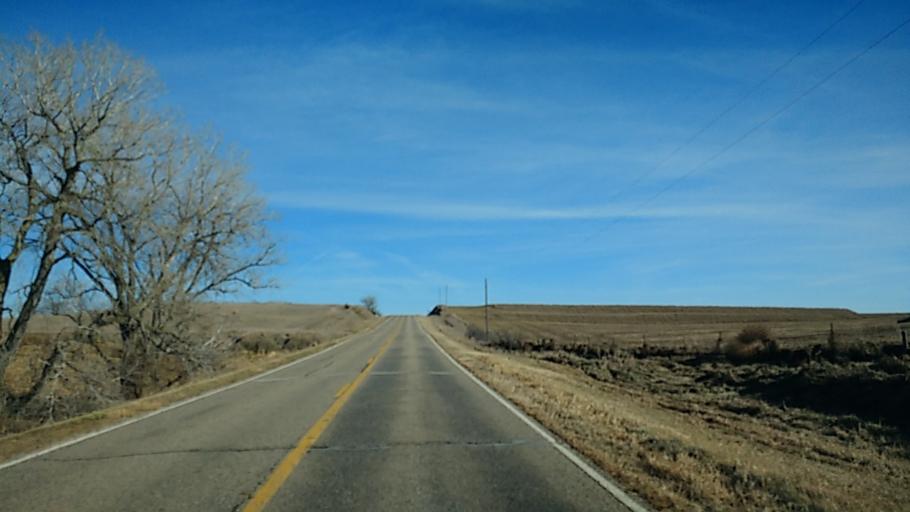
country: US
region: Iowa
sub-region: Woodbury County
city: Moville
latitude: 42.4004
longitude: -96.1365
